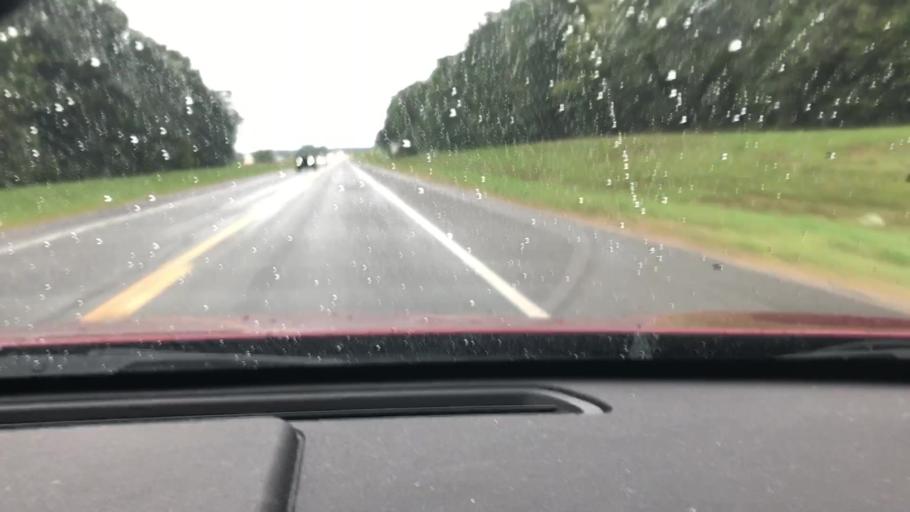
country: US
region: Arkansas
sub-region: Columbia County
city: Magnolia
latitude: 33.2967
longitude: -93.2475
